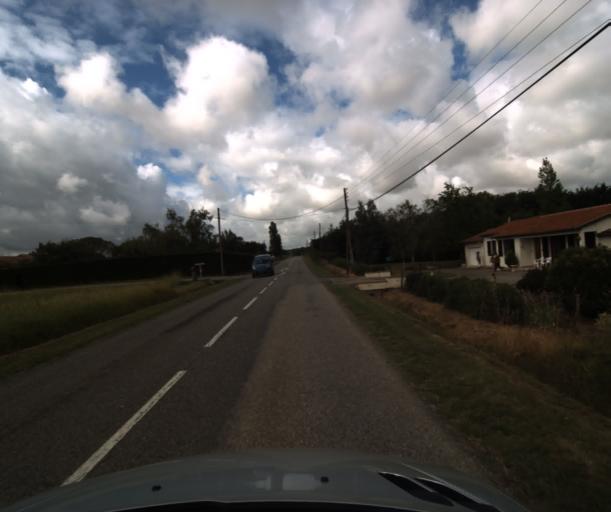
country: FR
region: Midi-Pyrenees
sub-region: Departement du Tarn-et-Garonne
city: Lavit
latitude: 43.9749
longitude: 0.9535
